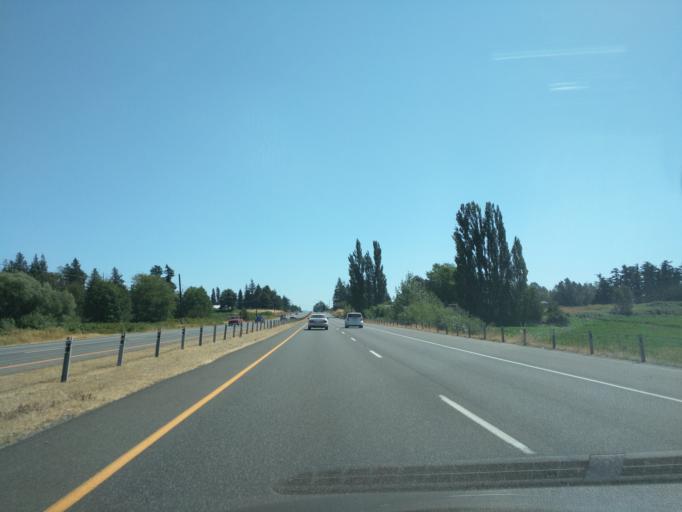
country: US
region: Washington
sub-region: Whatcom County
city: Lynden
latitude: 48.9141
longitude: -122.4858
